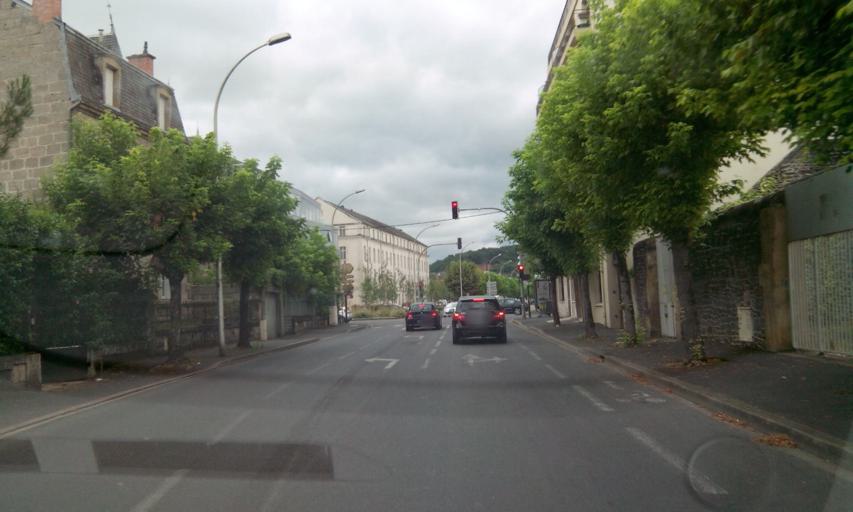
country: FR
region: Limousin
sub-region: Departement de la Correze
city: Brive-la-Gaillarde
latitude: 45.1547
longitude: 1.5390
